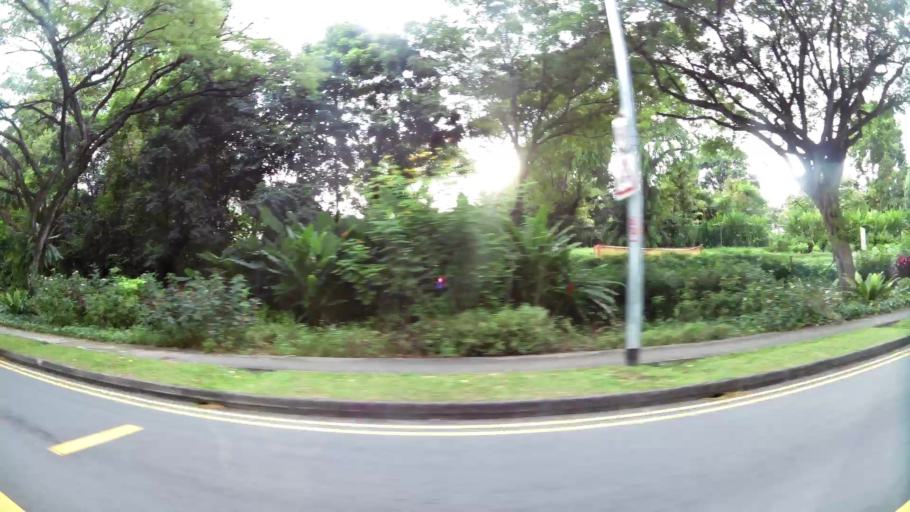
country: SG
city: Singapore
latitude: 1.2796
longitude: 103.8028
